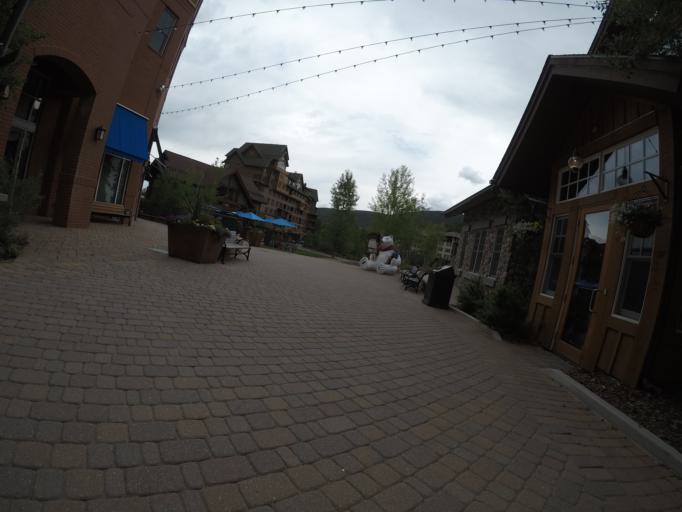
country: US
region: Colorado
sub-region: Grand County
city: Fraser
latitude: 39.8843
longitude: -105.7620
